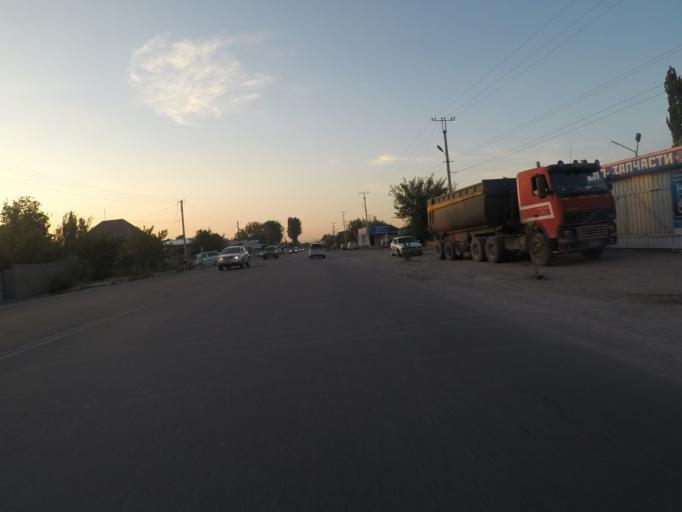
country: KG
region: Chuy
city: Lebedinovka
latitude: 42.8071
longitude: 74.6473
